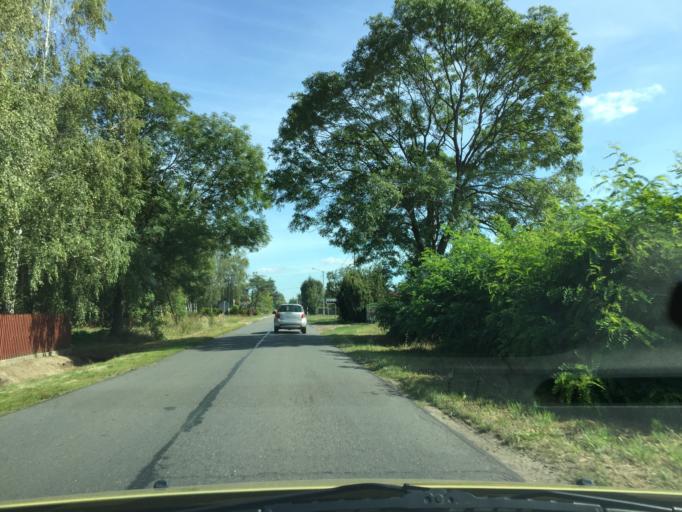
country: PL
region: Greater Poland Voivodeship
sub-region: Powiat kaliski
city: Zelazkow
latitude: 51.9430
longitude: 18.2029
